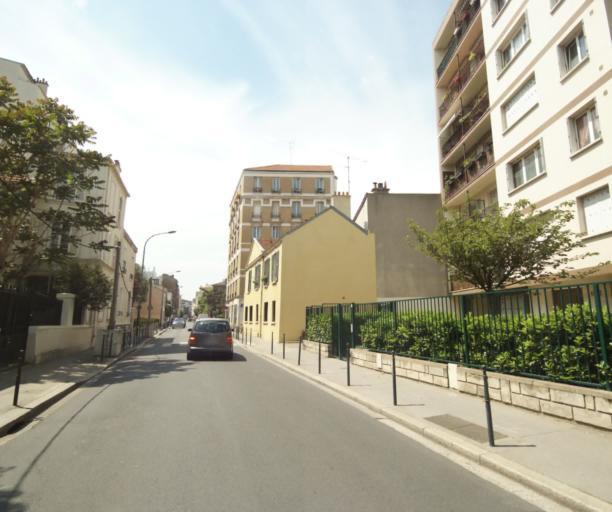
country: FR
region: Ile-de-France
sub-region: Departement des Hauts-de-Seine
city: Bois-Colombes
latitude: 48.9093
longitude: 2.2712
